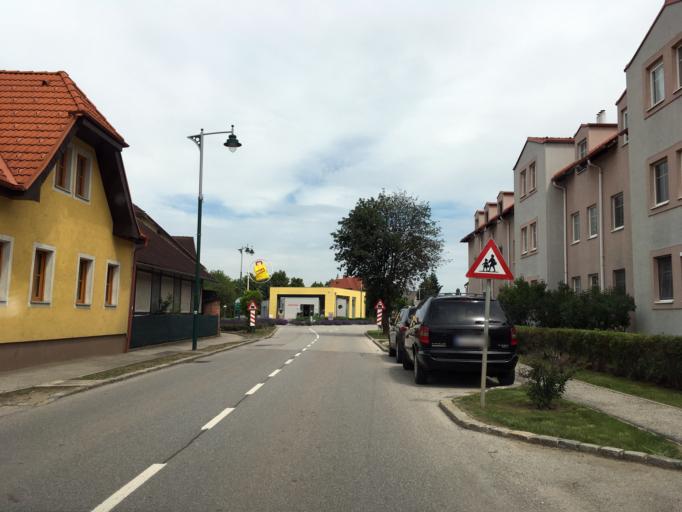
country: AT
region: Lower Austria
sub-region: Politischer Bezirk Wiener Neustadt
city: Bad Erlach
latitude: 47.7305
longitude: 16.2134
